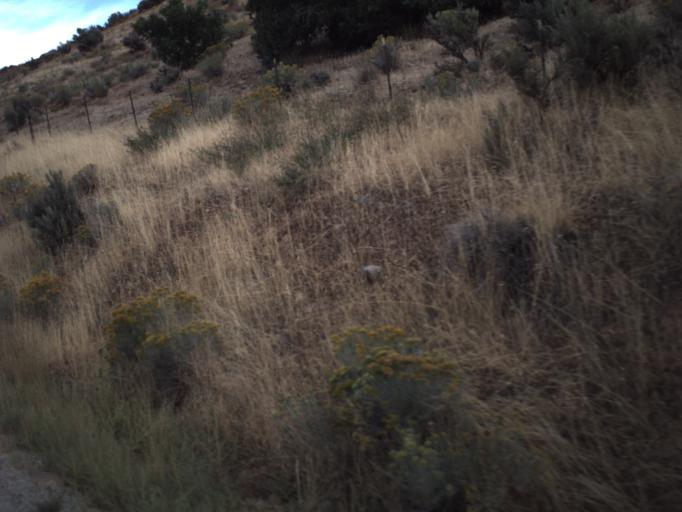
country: US
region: Utah
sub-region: Morgan County
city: Morgan
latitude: 41.0463
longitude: -111.6706
